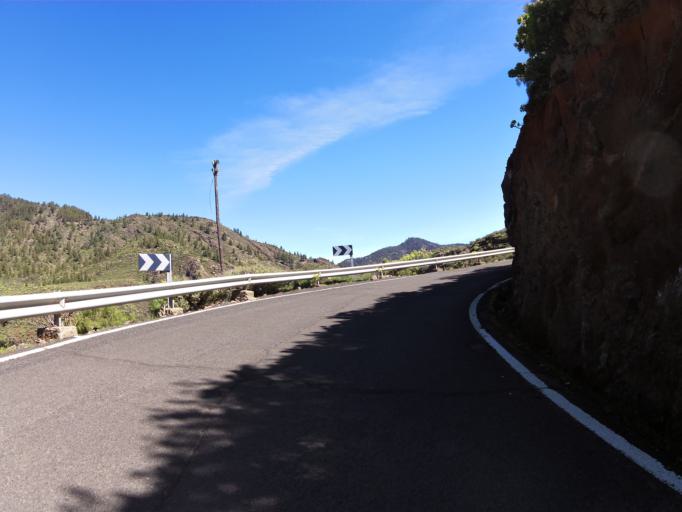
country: ES
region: Canary Islands
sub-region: Provincia de Las Palmas
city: Artenara
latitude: 28.0105
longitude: -15.6869
